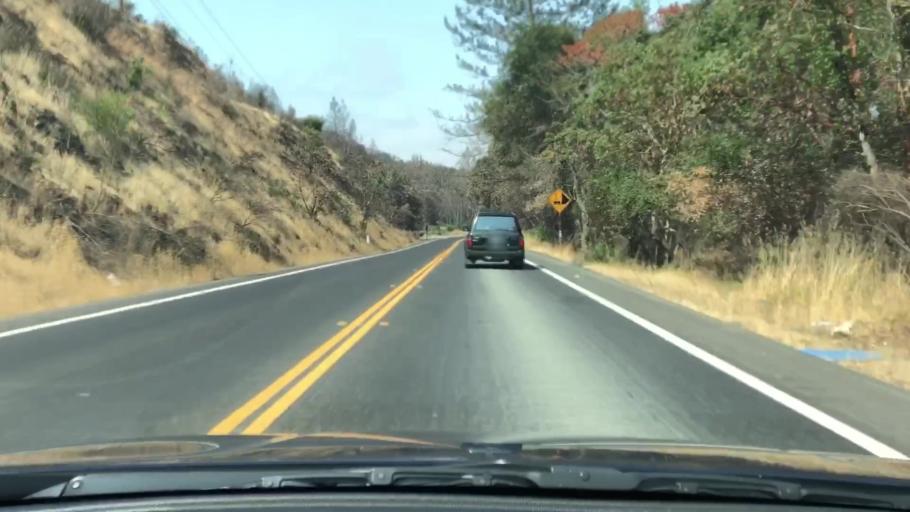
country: US
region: California
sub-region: Sonoma County
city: Larkfield-Wikiup
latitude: 38.5056
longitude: -122.7270
